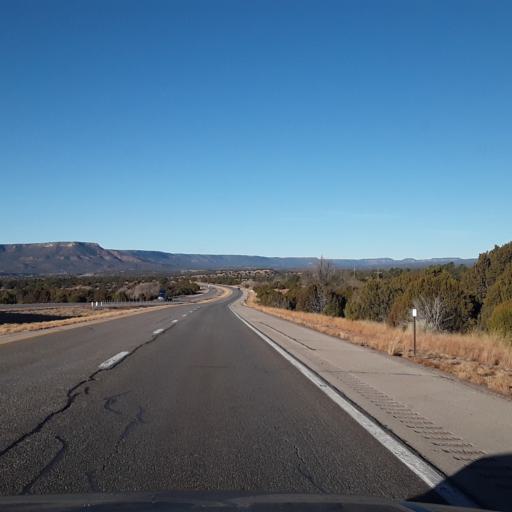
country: US
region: New Mexico
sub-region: San Miguel County
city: Las Vegas
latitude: 35.3972
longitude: -105.3882
